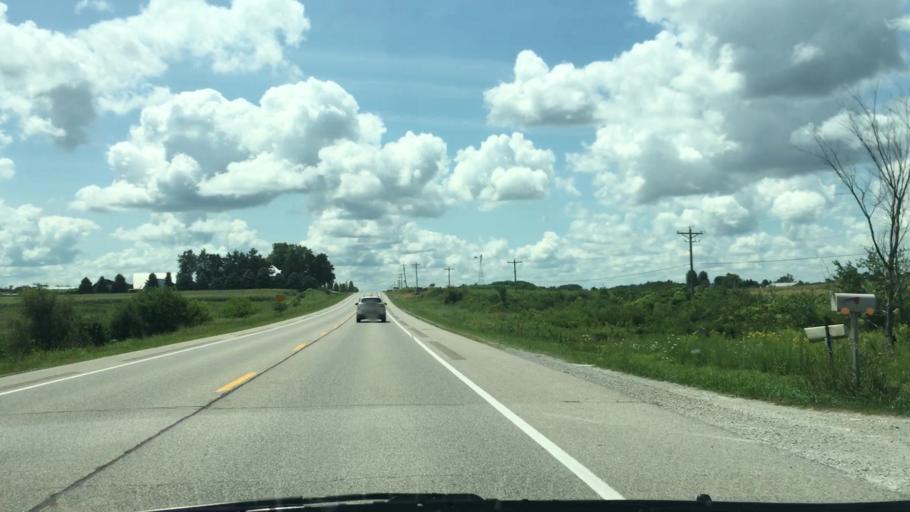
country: US
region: Iowa
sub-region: Johnson County
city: Solon
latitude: 41.7256
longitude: -91.4775
